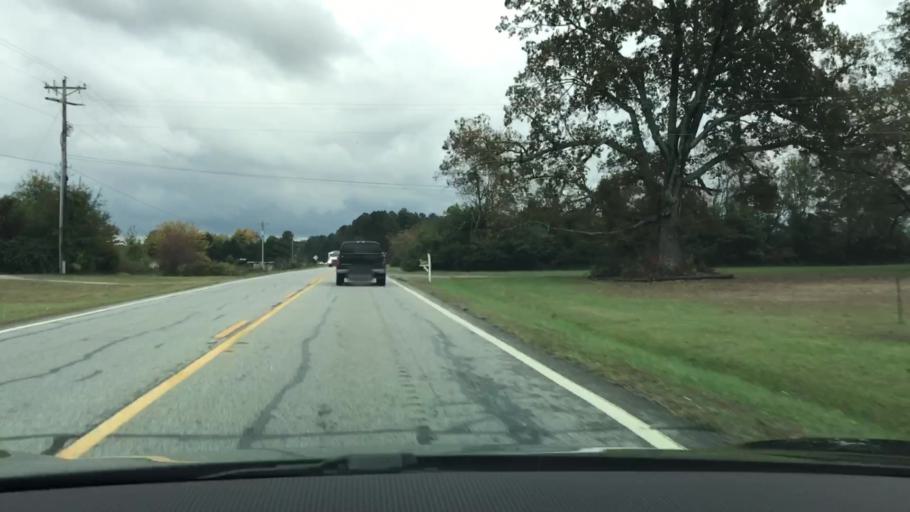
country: US
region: Georgia
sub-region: Oconee County
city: Watkinsville
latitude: 33.8176
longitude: -83.3638
